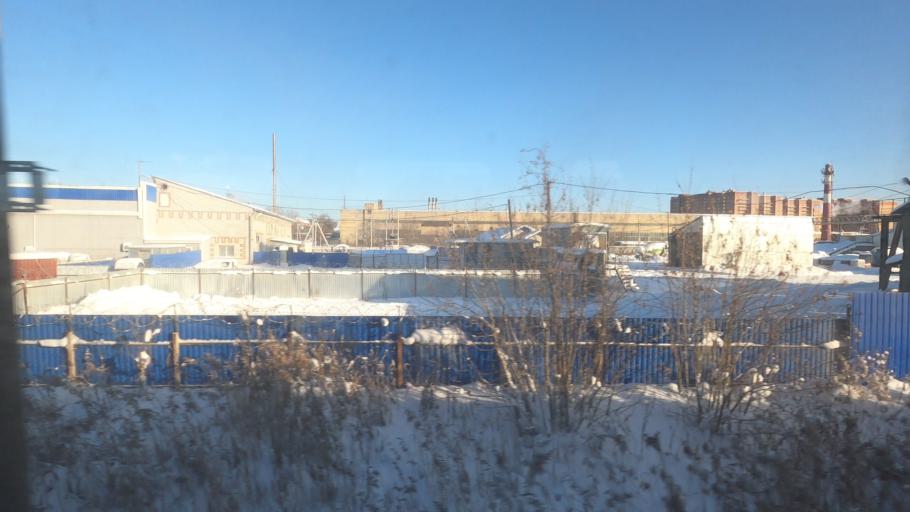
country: RU
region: Moskovskaya
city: Dmitrov
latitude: 56.3757
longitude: 37.5220
